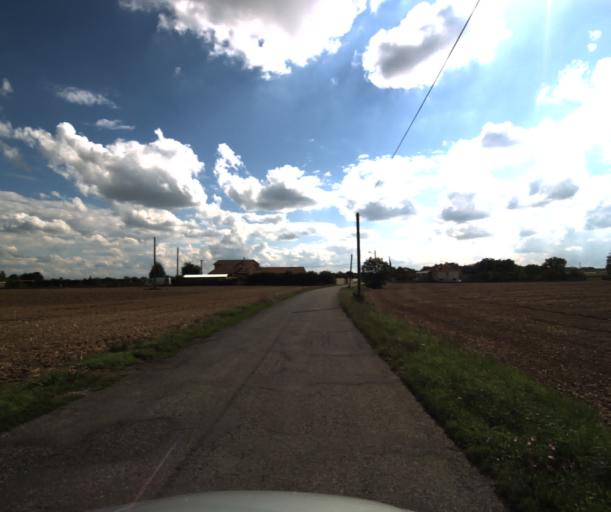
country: FR
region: Midi-Pyrenees
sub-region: Departement de la Haute-Garonne
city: Saubens
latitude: 43.4808
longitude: 1.3673
